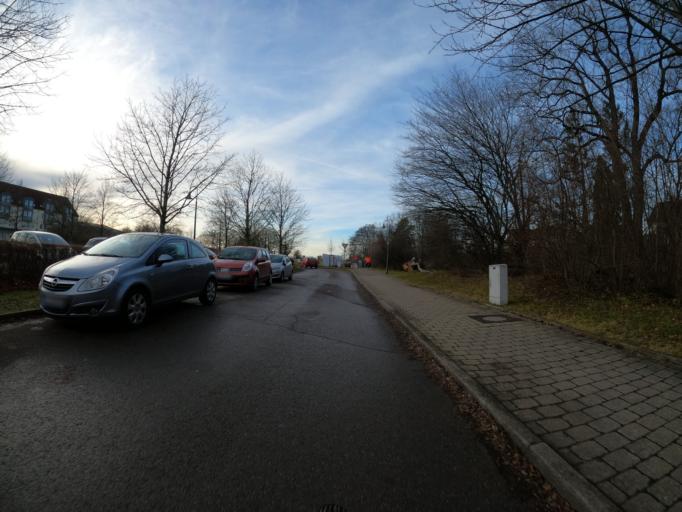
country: DE
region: Baden-Wuerttemberg
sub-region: Regierungsbezirk Stuttgart
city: Boll
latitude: 48.6395
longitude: 9.5975
